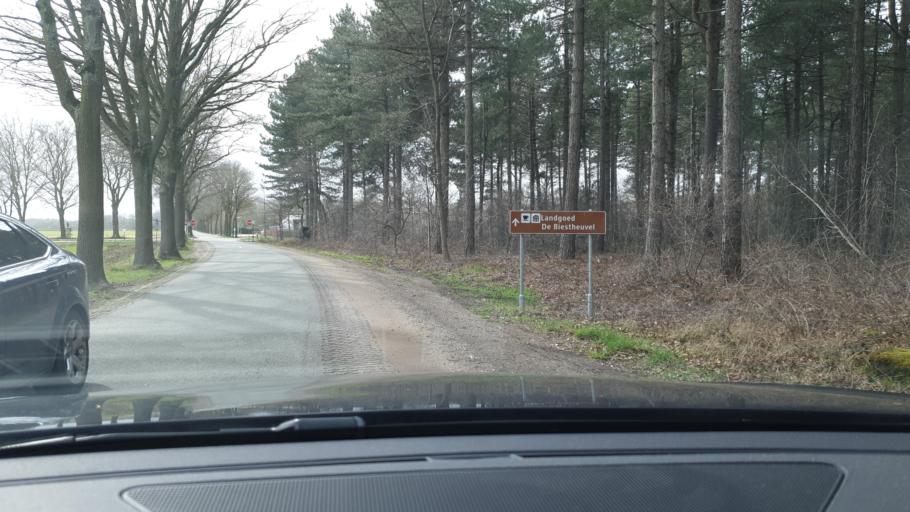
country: NL
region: North Brabant
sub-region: Gemeente Eersel
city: Eersel
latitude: 51.4085
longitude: 5.3143
